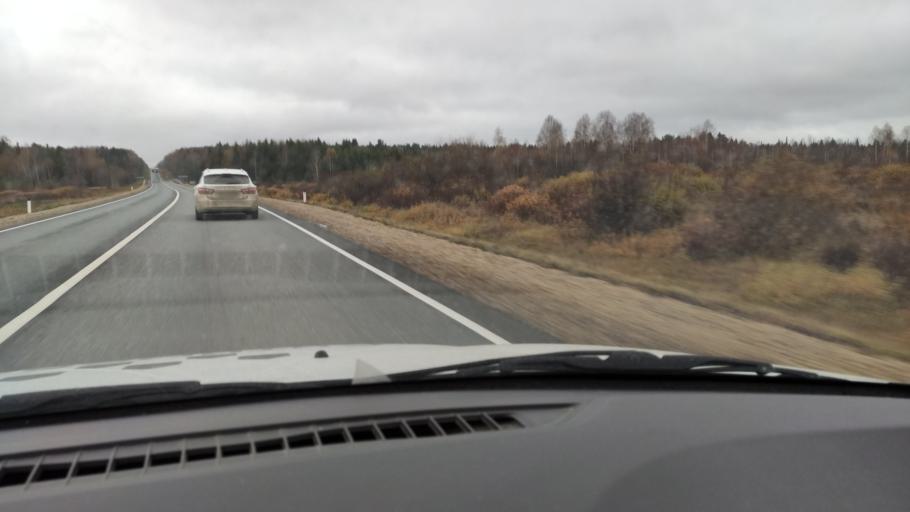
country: RU
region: Kirov
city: Chernaya Kholunitsa
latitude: 58.8591
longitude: 51.6958
